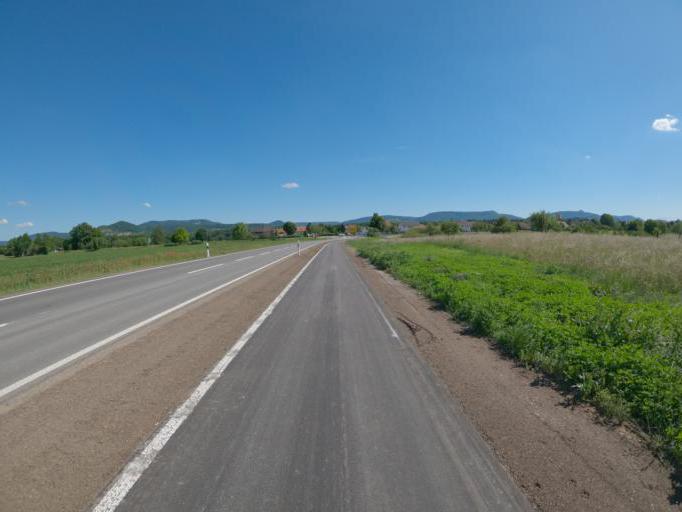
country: DE
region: Baden-Wuerttemberg
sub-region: Regierungsbezirk Stuttgart
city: Ohmden
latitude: 48.6513
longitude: 9.5369
